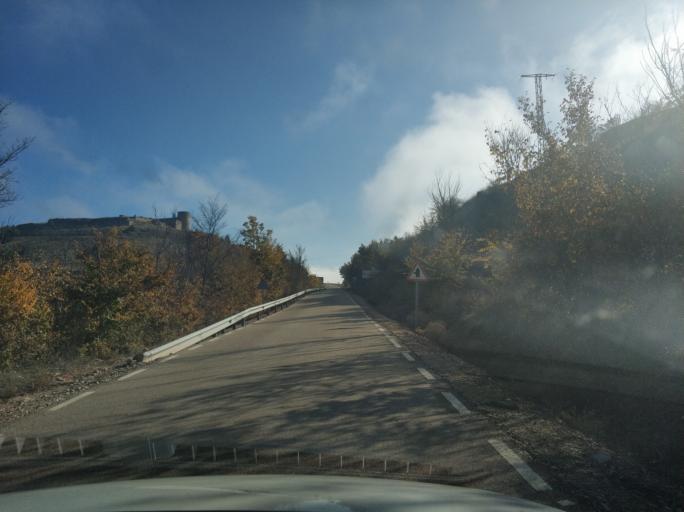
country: ES
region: Castille and Leon
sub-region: Provincia de Soria
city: Medinaceli
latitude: 41.1698
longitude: -2.4411
